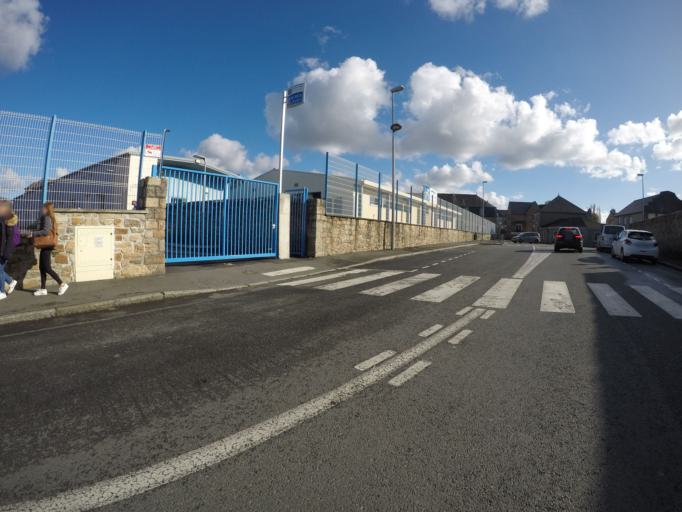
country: FR
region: Brittany
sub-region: Departement des Cotes-d'Armor
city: Guingamp
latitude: 48.5616
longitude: -3.1444
